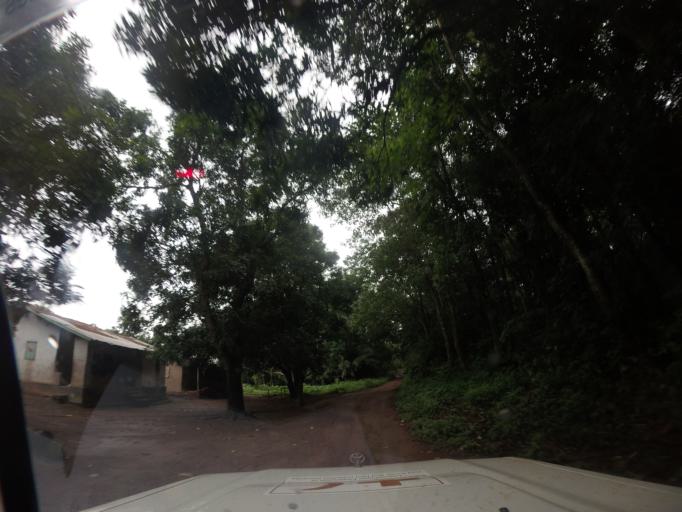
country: SL
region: Northern Province
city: Kamakwie
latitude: 9.6102
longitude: -12.2130
